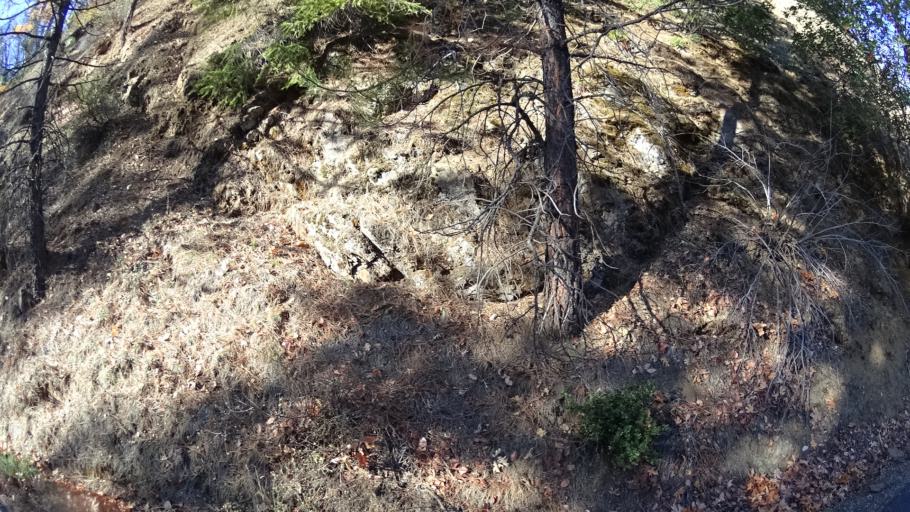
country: US
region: California
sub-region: Siskiyou County
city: Yreka
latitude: 41.9109
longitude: -122.8365
